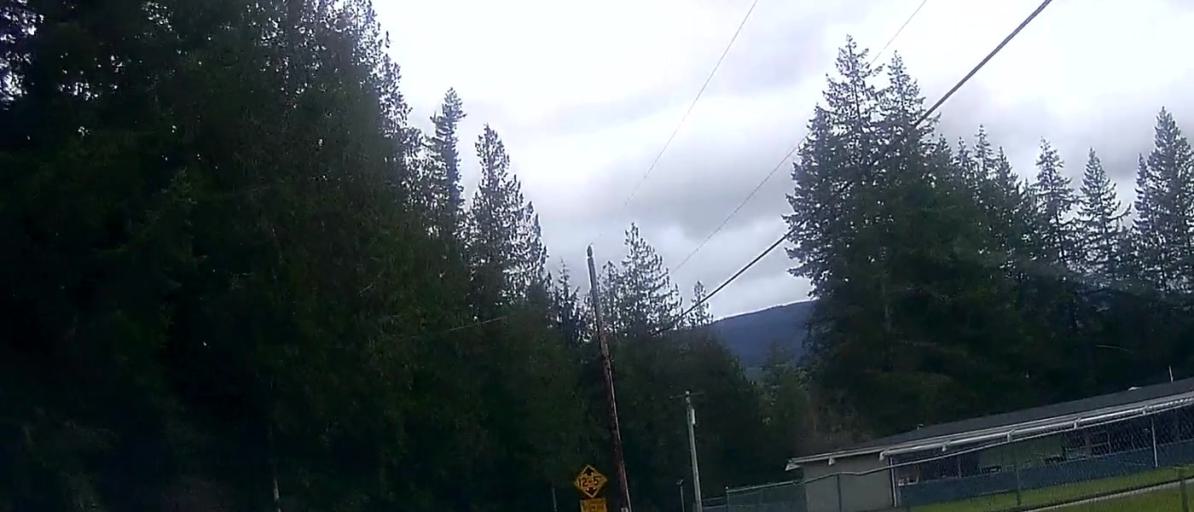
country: US
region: Washington
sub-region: Skagit County
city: Sedro-Woolley
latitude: 48.5855
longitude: -122.2249
